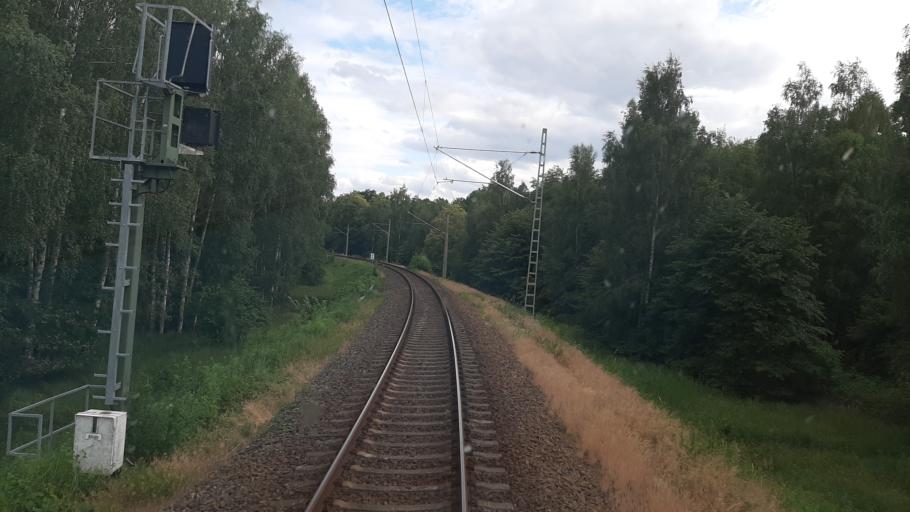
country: DE
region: Brandenburg
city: Brieselang
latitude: 52.5804
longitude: 13.0260
